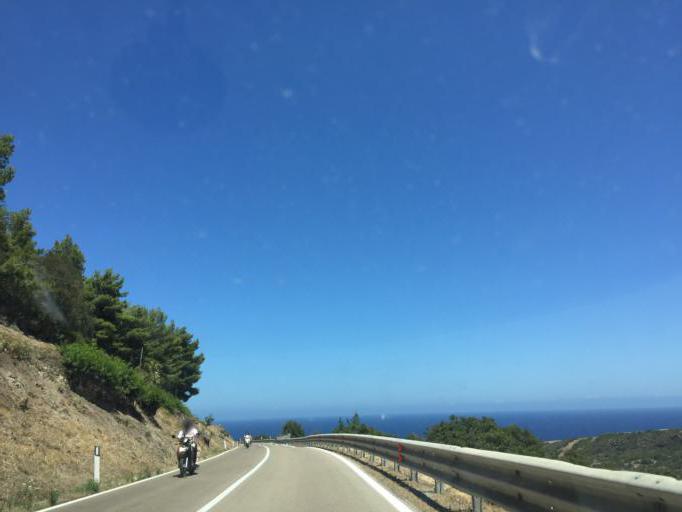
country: IT
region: Sardinia
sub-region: Provincia di Sassari
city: Castelsardo
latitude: 40.9046
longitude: 8.7390
